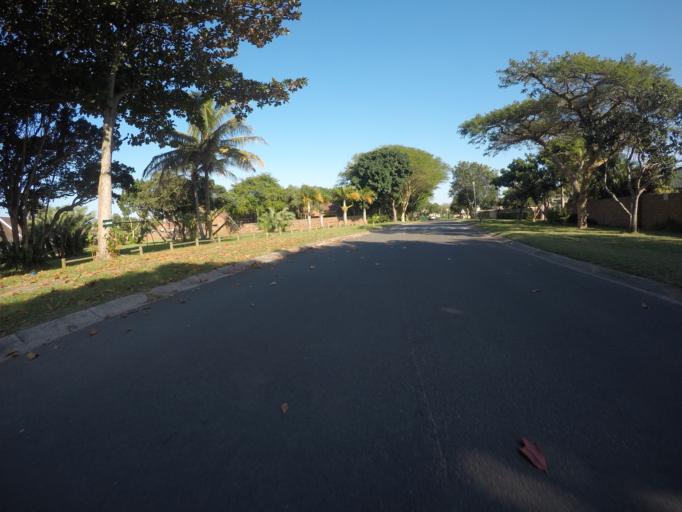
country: ZA
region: KwaZulu-Natal
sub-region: uThungulu District Municipality
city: Richards Bay
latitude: -28.7875
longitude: 32.1004
